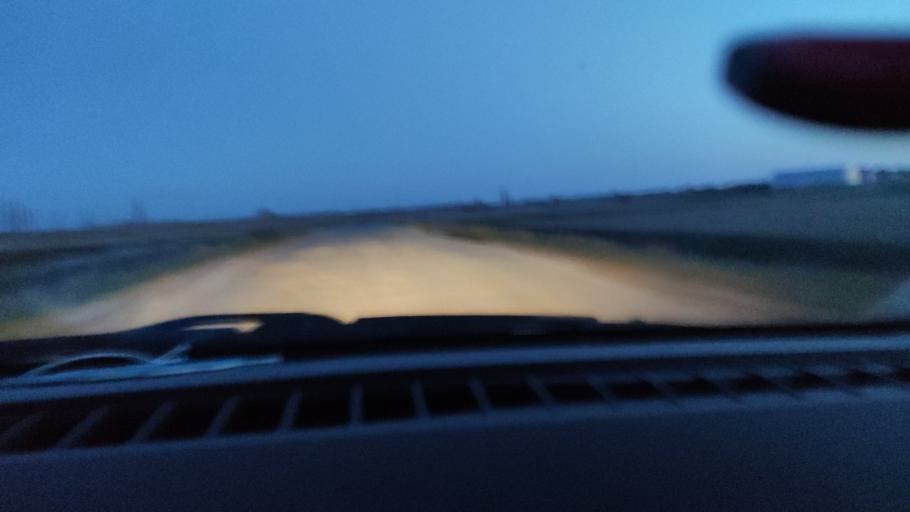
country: RU
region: Saratov
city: Rovnoye
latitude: 50.9348
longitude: 46.0945
